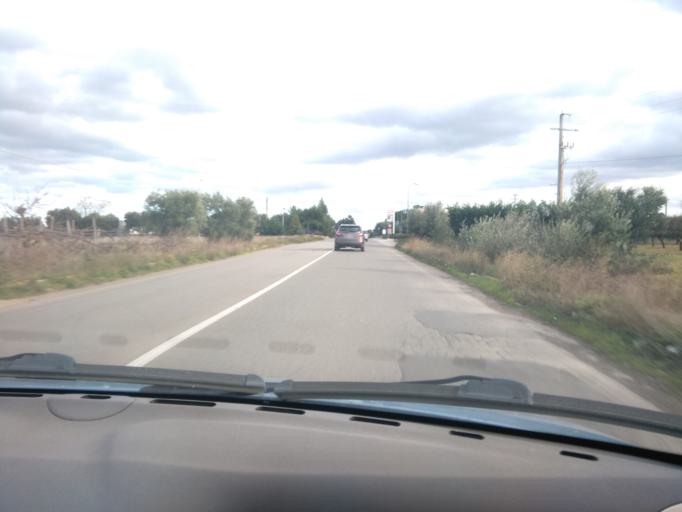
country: IT
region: Apulia
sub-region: Provincia di Bari
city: Adelfia
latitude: 41.0030
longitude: 16.9010
